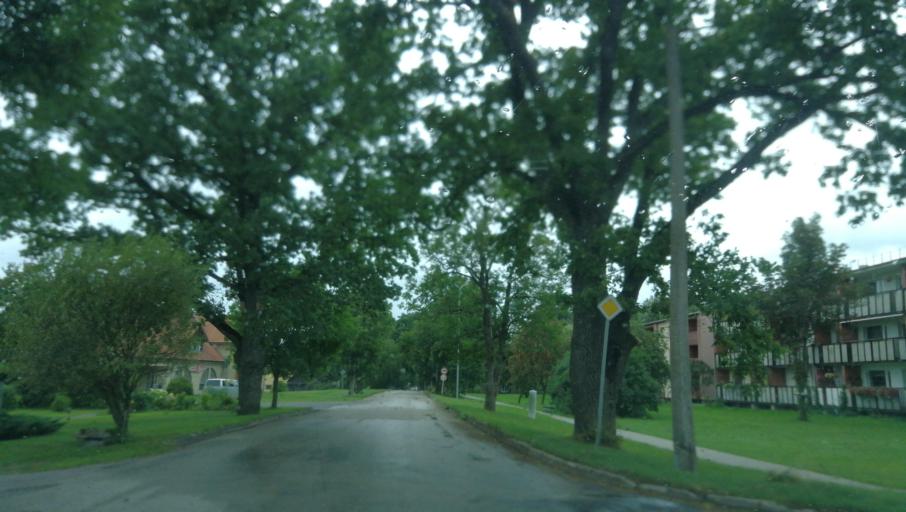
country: LV
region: Beverina
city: Murmuiza
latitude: 57.4728
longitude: 25.4923
